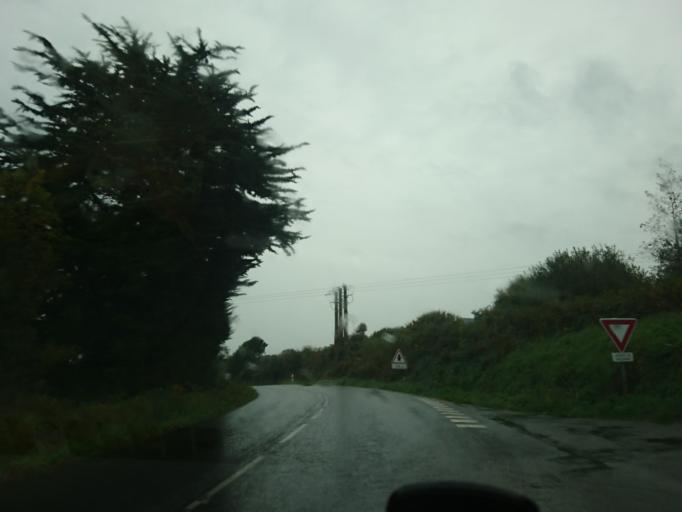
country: FR
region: Brittany
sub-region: Departement du Finistere
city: Plouguerneau
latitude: 48.5938
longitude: -4.5124
